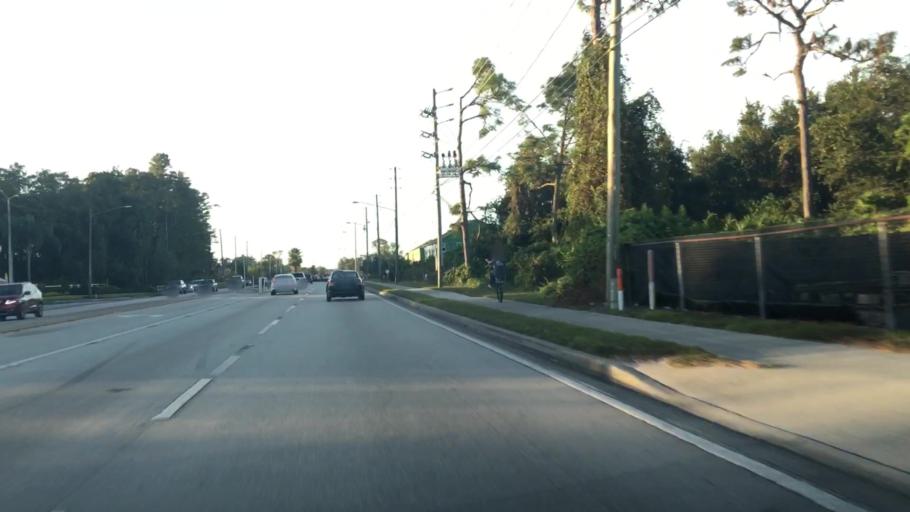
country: US
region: Florida
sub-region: Orange County
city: Conway
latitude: 28.4868
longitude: -81.2855
